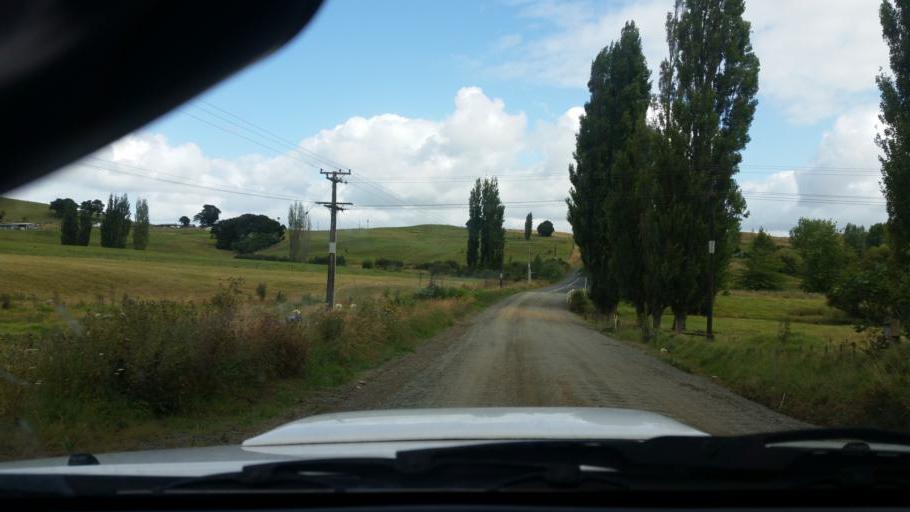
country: NZ
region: Auckland
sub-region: Auckland
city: Wellsford
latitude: -36.1330
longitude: 174.3602
